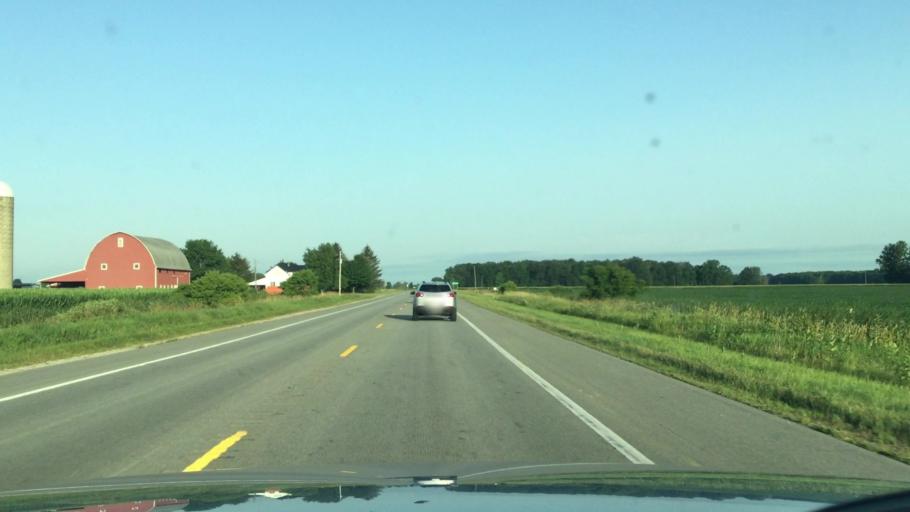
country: US
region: Michigan
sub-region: Montcalm County
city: Carson City
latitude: 43.1761
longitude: -84.7223
